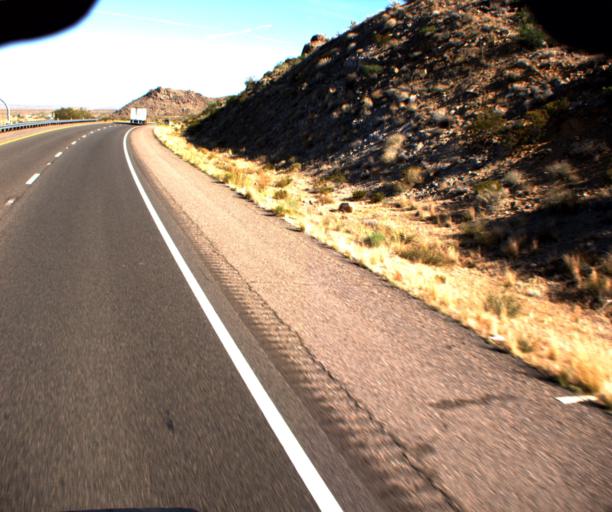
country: US
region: Arizona
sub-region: Mohave County
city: Golden Valley
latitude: 35.2289
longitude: -114.1351
